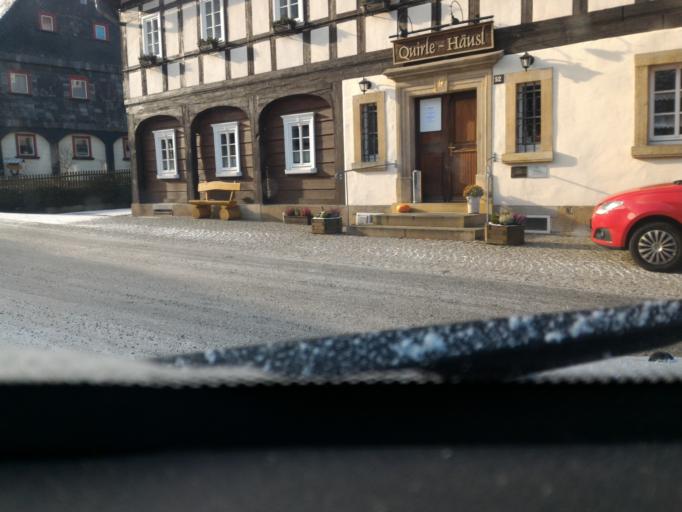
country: DE
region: Saxony
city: Grossschonau
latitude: 50.8661
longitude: 14.6499
